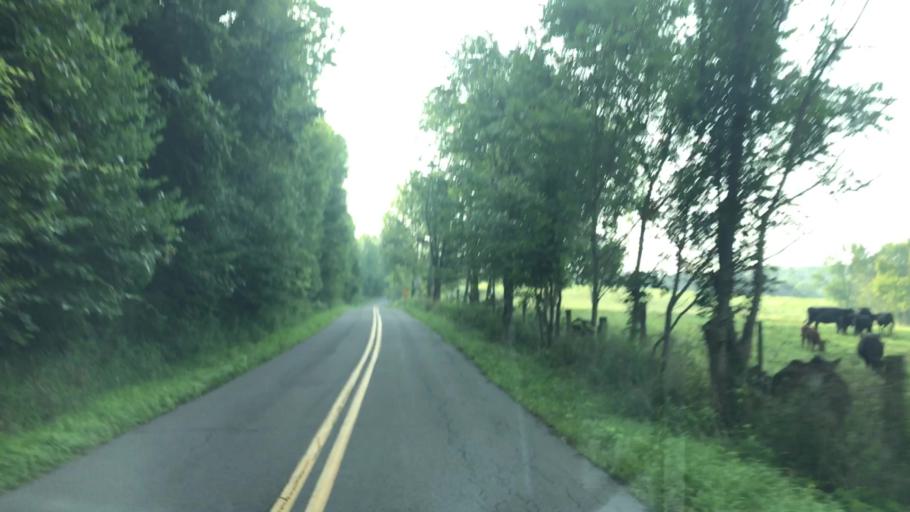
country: US
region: Pennsylvania
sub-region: Wyoming County
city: Factoryville
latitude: 41.6103
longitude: -75.7366
